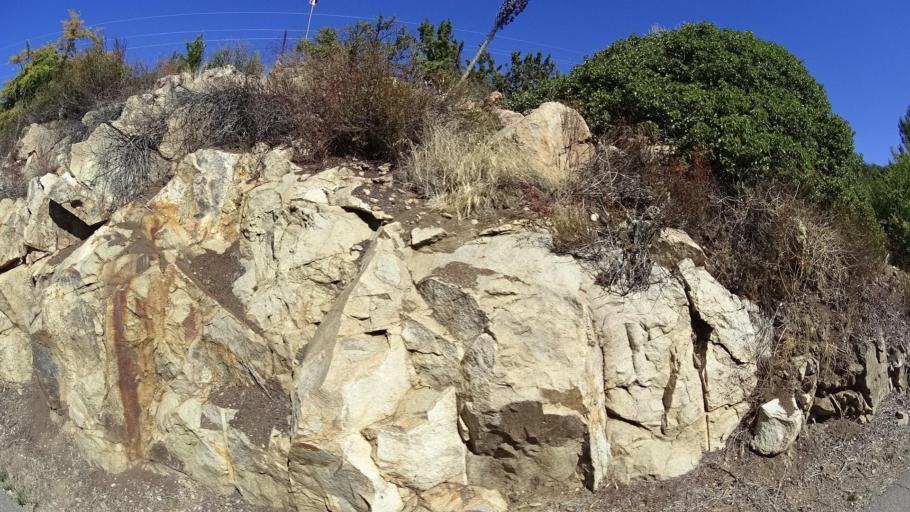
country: US
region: California
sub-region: San Diego County
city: Descanso
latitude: 32.8068
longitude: -116.6380
